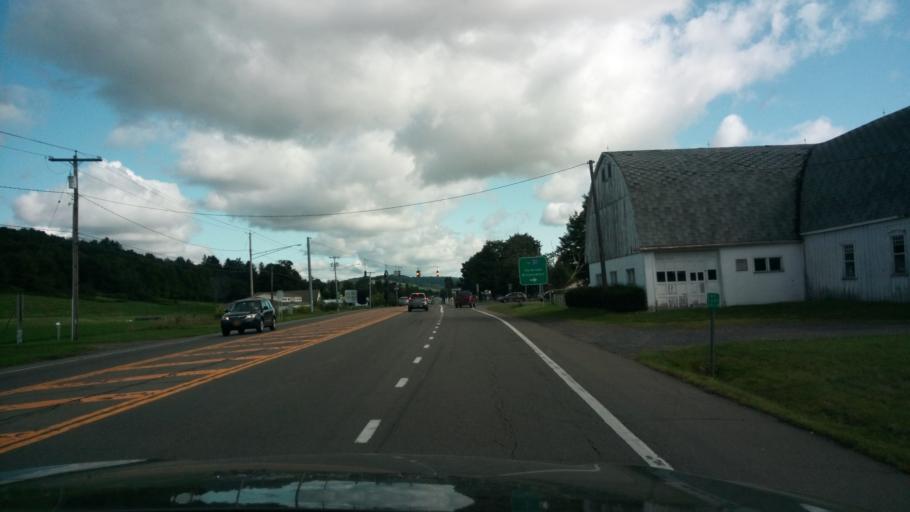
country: US
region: New York
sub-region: Cortland County
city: Homer
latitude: 42.6267
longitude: -76.1921
